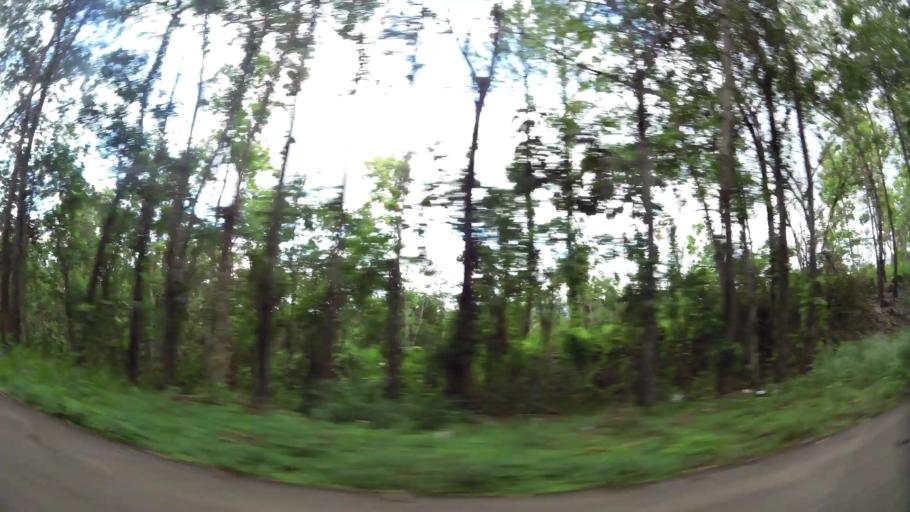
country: DO
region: Monsenor Nouel
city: Sabana del Puerto
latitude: 19.0888
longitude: -70.4379
